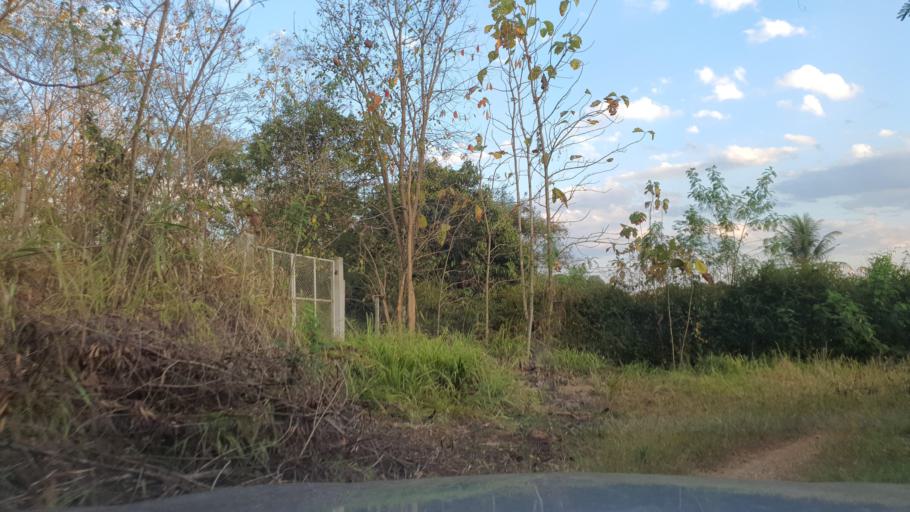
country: TH
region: Chiang Mai
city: Hang Dong
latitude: 18.7328
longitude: 98.8772
